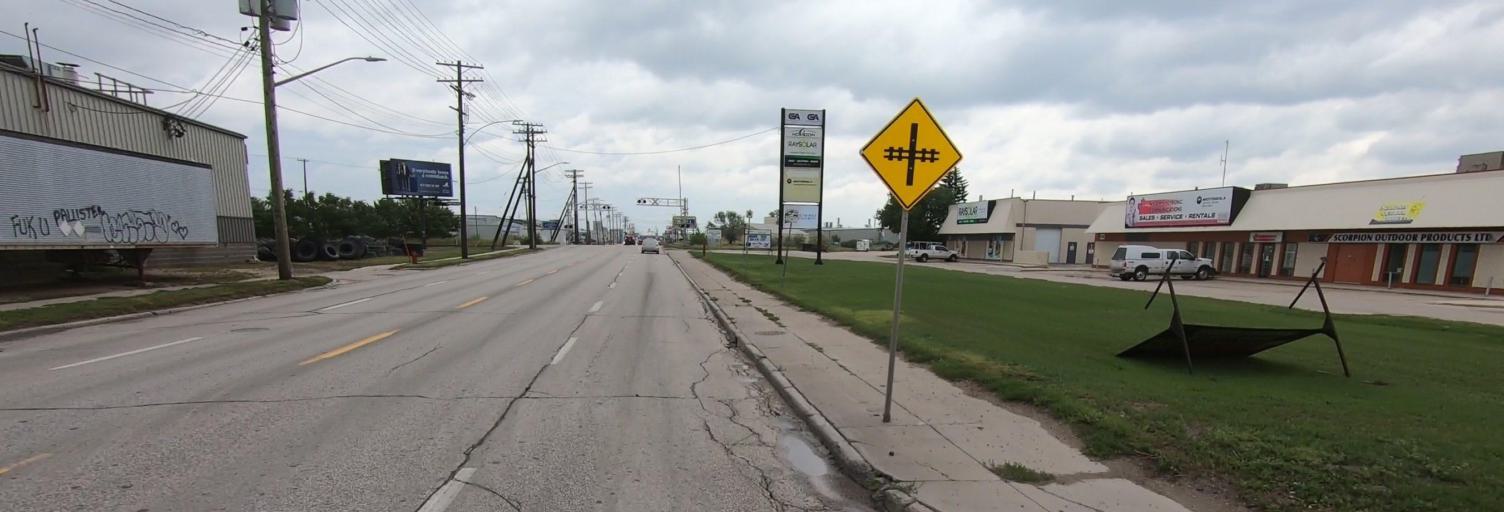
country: CA
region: Manitoba
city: Winnipeg
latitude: 49.8819
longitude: -97.0877
